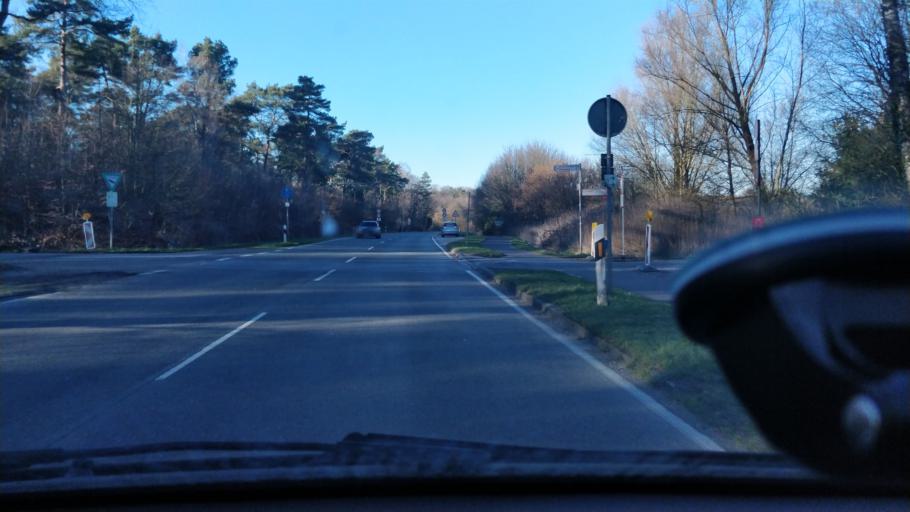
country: DE
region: North Rhine-Westphalia
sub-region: Regierungsbezirk Munster
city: Bottrop
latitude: 51.5637
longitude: 6.8711
